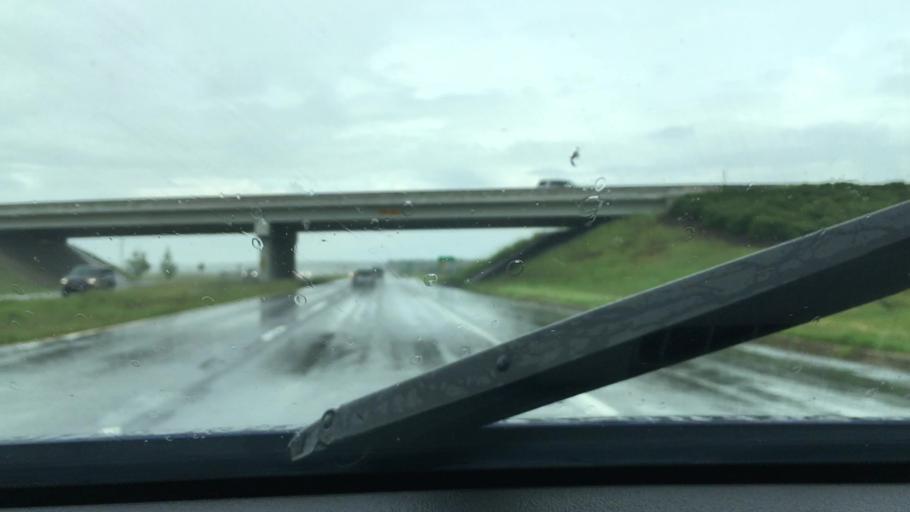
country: US
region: South Carolina
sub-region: Sumter County
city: Oakland
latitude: 33.9539
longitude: -80.4915
